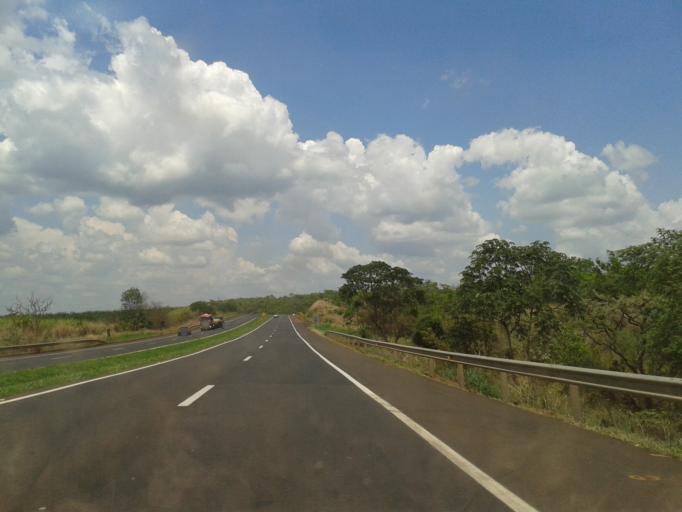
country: BR
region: Minas Gerais
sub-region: Araguari
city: Araguari
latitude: -18.7204
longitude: -48.2024
